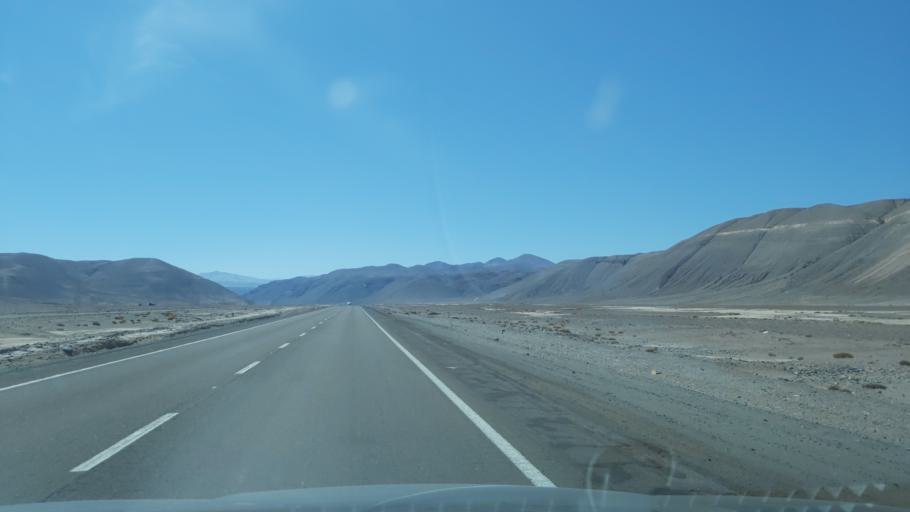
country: CL
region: Atacama
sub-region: Provincia de Chanaral
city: Diego de Almagro
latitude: -26.3513
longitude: -69.8884
